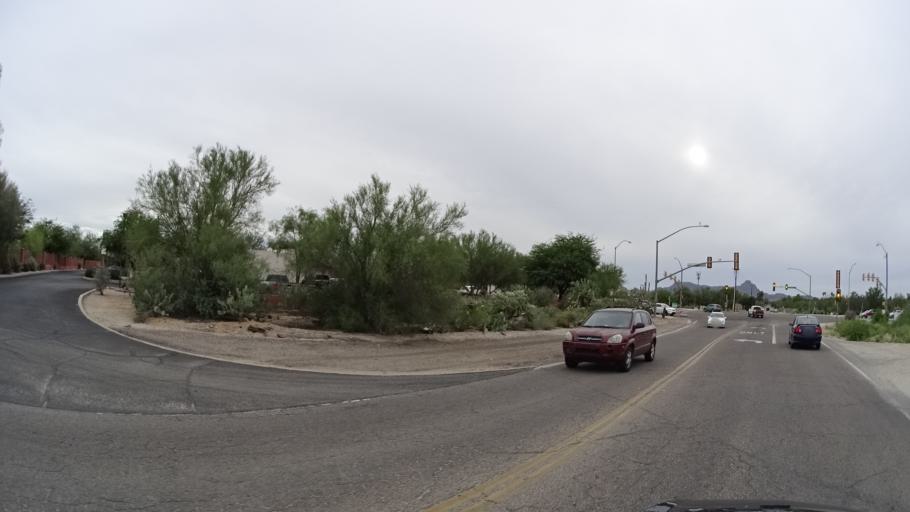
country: US
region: Arizona
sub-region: Pima County
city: Casas Adobes
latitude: 32.3518
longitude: -111.0459
